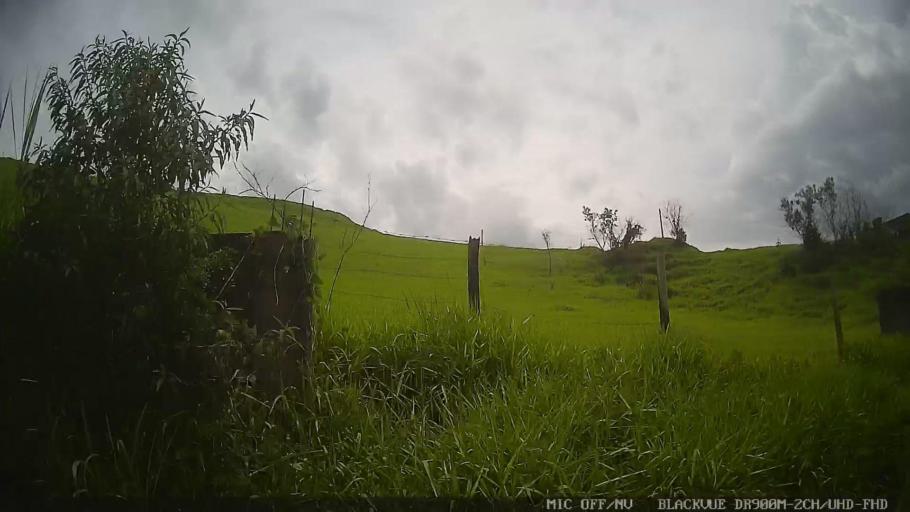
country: BR
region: Sao Paulo
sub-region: Santa Isabel
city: Santa Isabel
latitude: -23.3624
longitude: -46.2481
